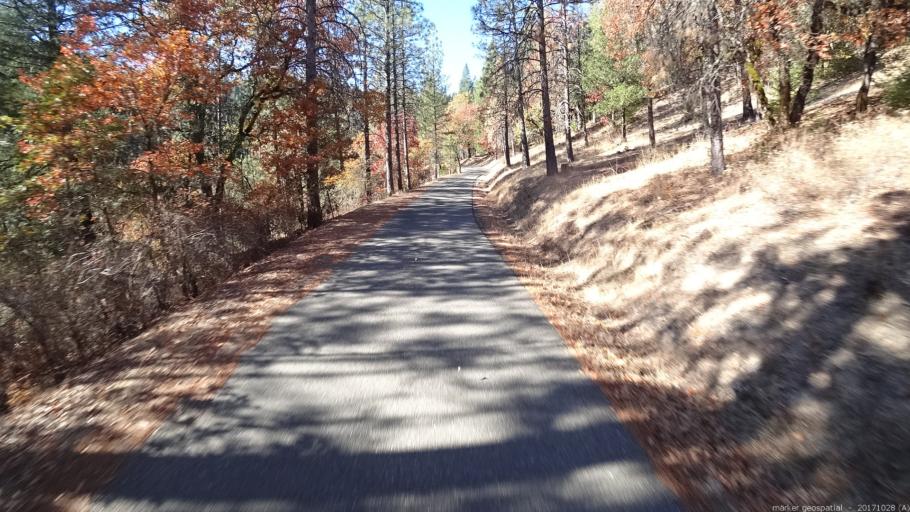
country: US
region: California
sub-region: Shasta County
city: Shasta
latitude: 40.7591
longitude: -122.5739
